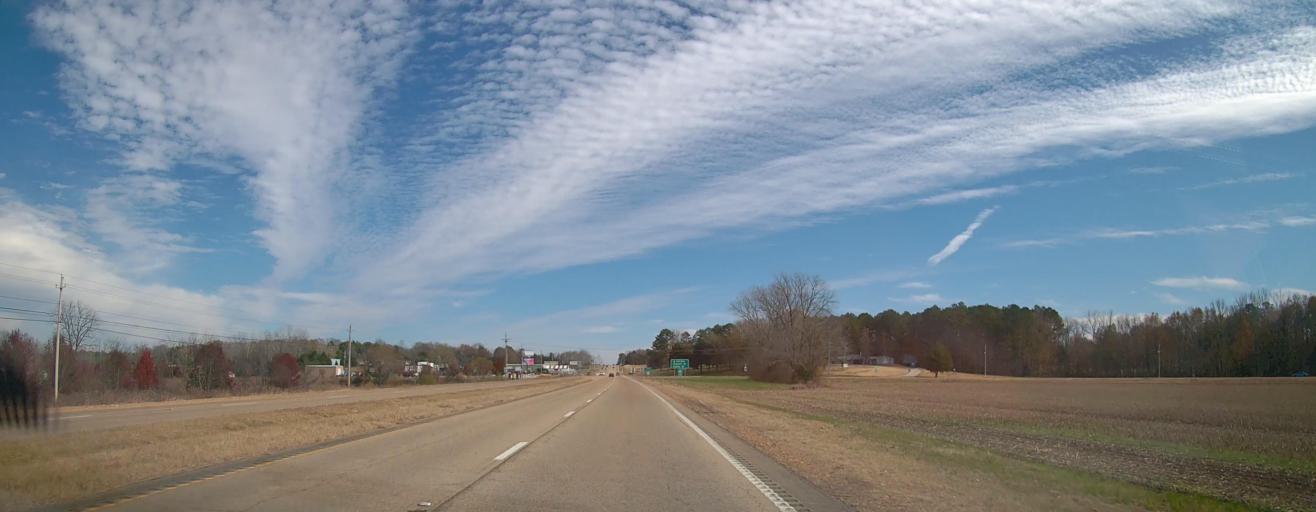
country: US
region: Mississippi
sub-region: Alcorn County
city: Corinth
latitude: 34.9310
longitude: -88.5744
